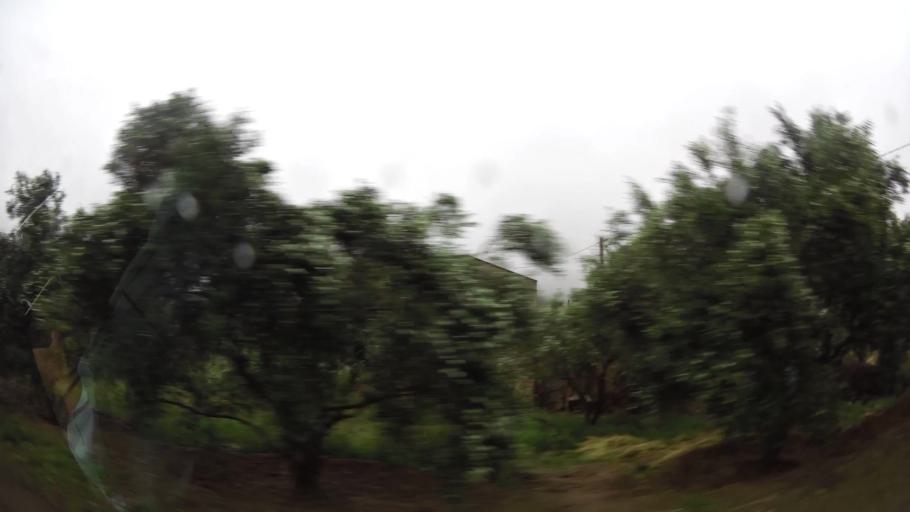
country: MA
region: Oriental
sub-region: Nador
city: Boudinar
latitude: 35.1175
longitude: -3.5764
